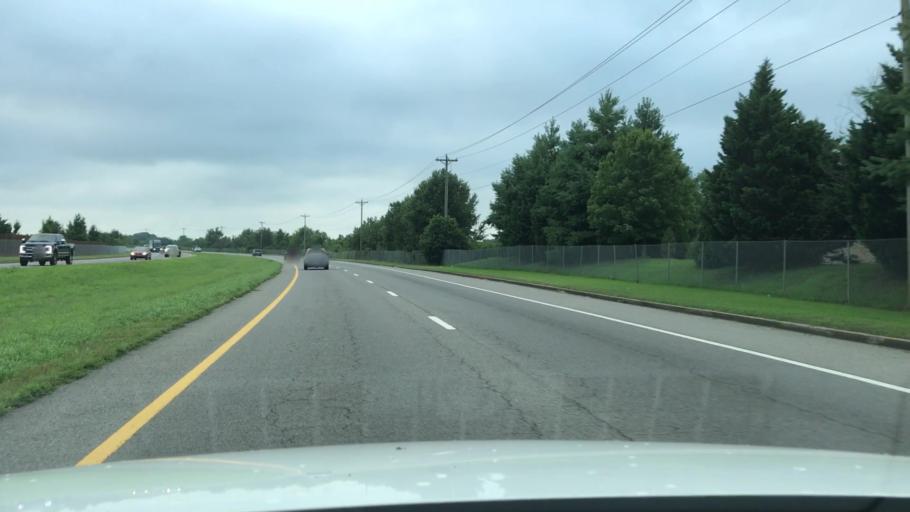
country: US
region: Tennessee
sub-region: Sumner County
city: Gallatin
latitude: 36.3654
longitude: -86.4569
